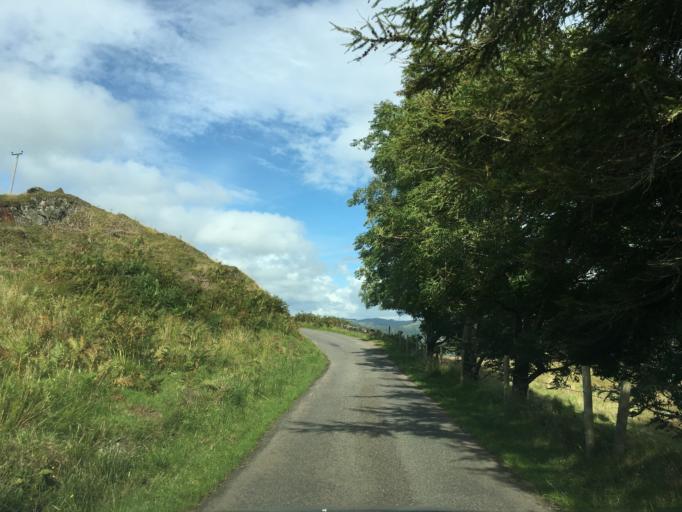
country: GB
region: Scotland
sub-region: Argyll and Bute
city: Oban
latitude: 56.2609
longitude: -5.6349
